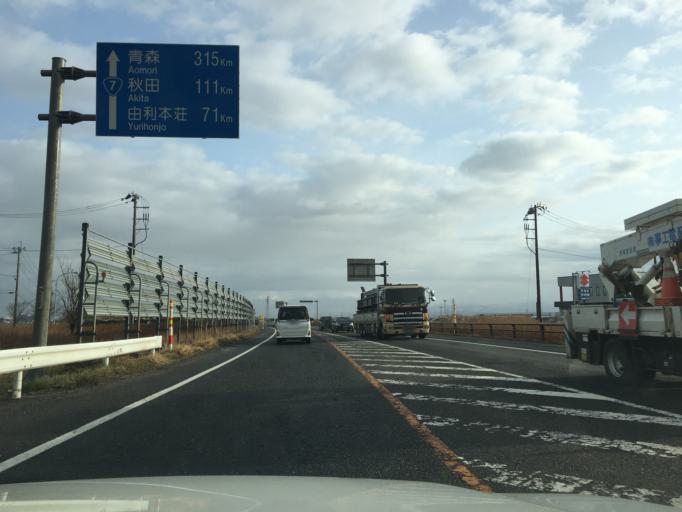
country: JP
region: Yamagata
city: Sakata
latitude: 38.8299
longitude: 139.8459
